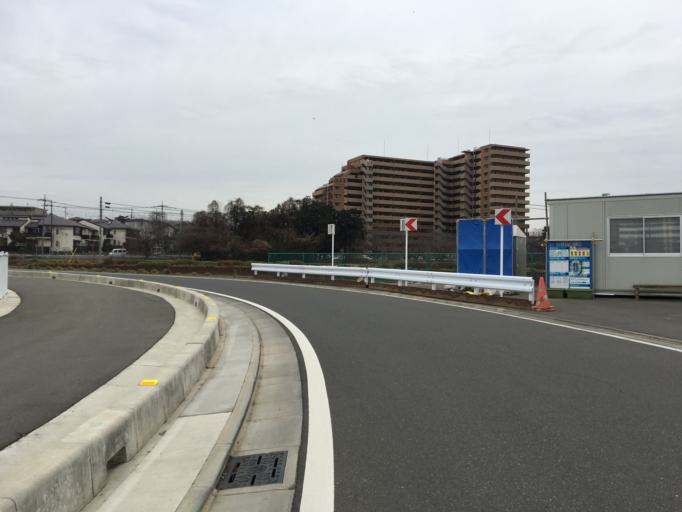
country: JP
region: Saitama
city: Tokorozawa
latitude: 35.8043
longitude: 139.5121
